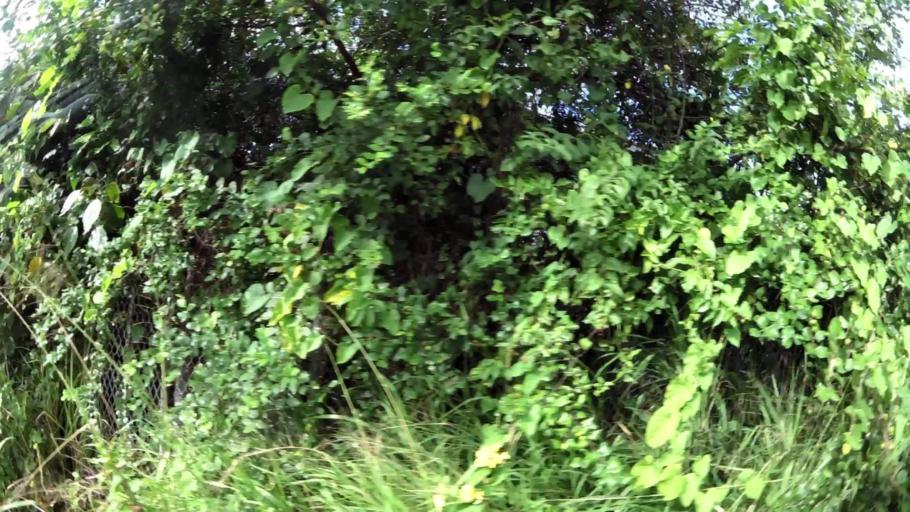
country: AG
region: Saint John
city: Saint John's
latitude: 17.1296
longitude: -61.8288
